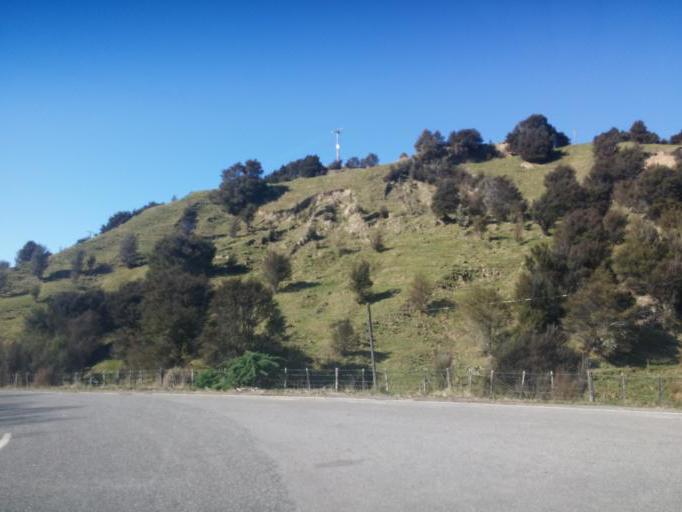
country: NZ
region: Wellington
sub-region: South Wairarapa District
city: Waipawa
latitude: -41.4176
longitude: 175.4867
